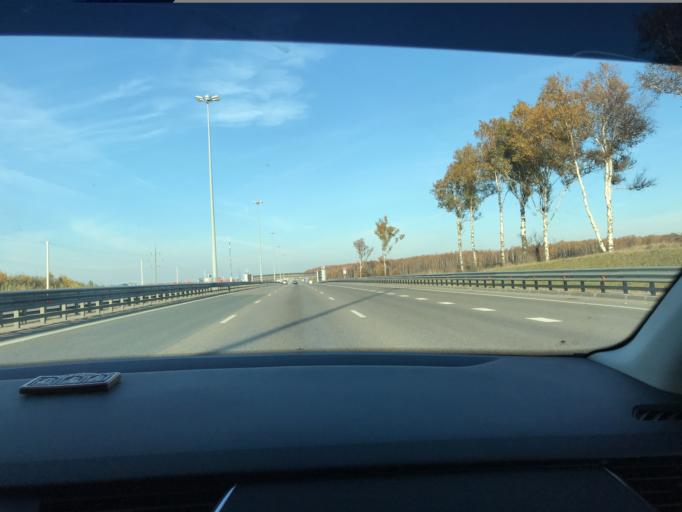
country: RU
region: Moscow
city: Khimki
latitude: 55.9324
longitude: 37.4011
